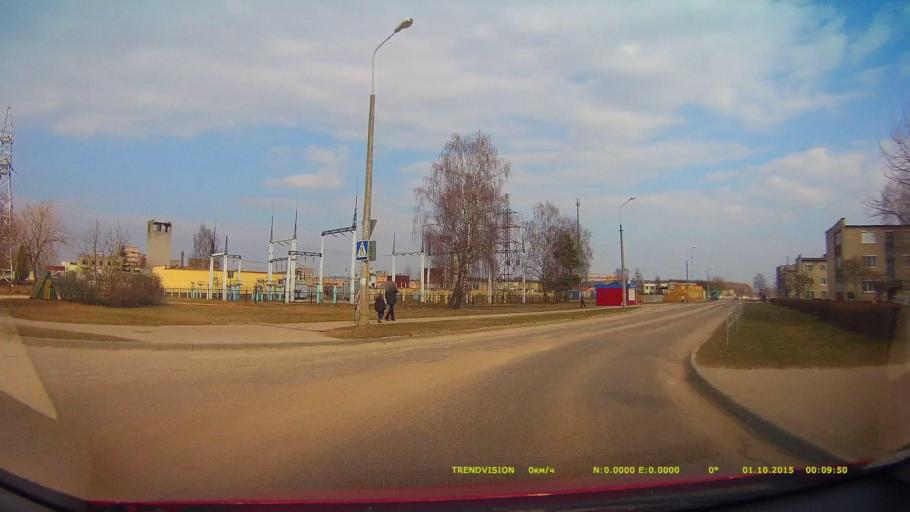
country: BY
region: Grodnenskaya
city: Lida
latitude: 53.9362
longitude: 25.2636
